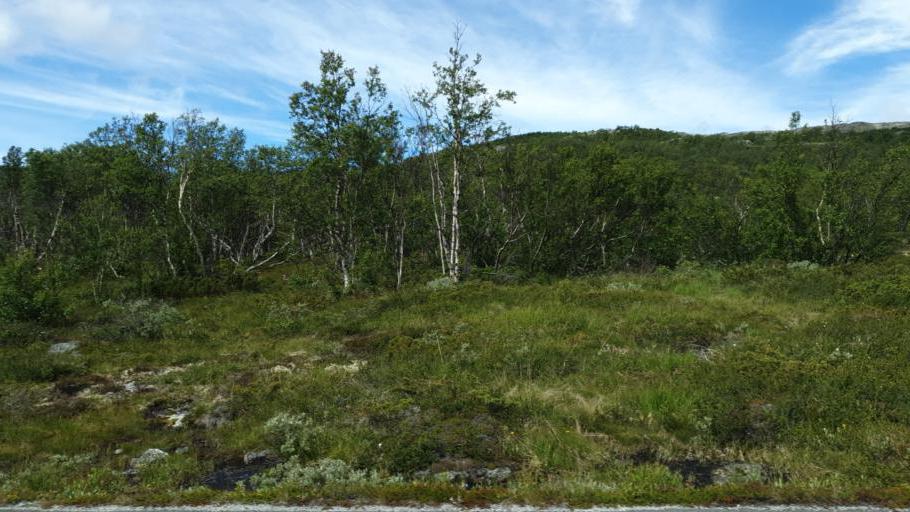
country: NO
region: Oppland
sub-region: Oystre Slidre
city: Heggenes
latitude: 61.4913
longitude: 8.8413
